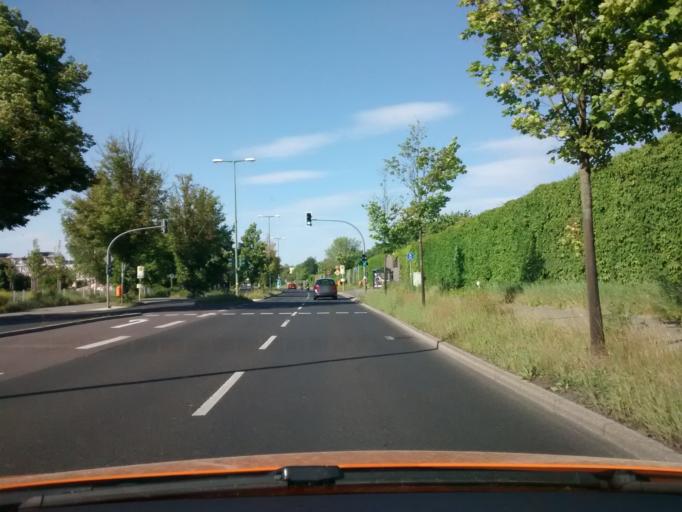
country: DE
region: Berlin
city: Marienfelde
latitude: 52.4049
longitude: 13.3560
